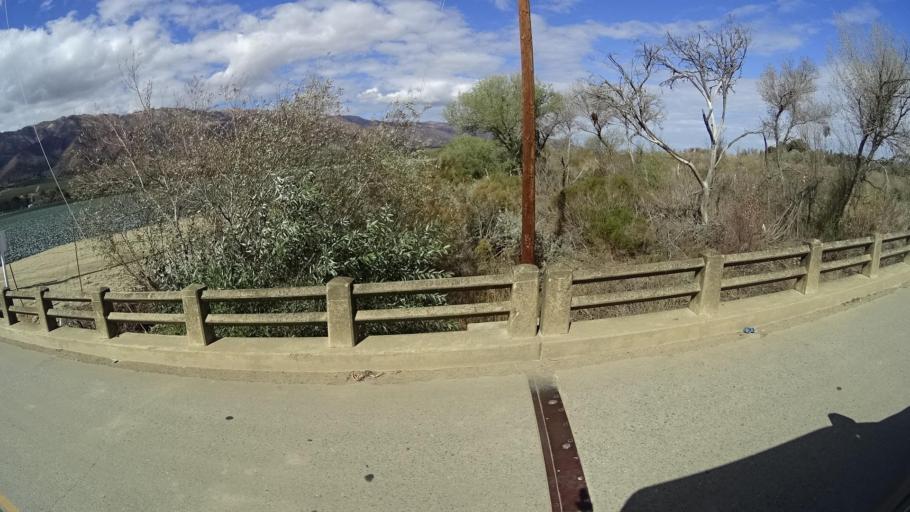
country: US
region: California
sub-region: Monterey County
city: Gonzales
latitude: 36.4839
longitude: -121.4704
